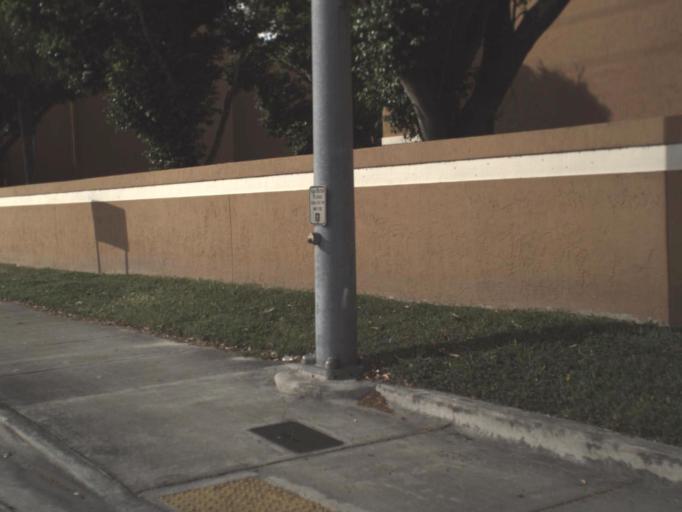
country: US
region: Florida
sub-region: Miami-Dade County
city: Three Lakes
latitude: 25.6270
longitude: -80.3932
